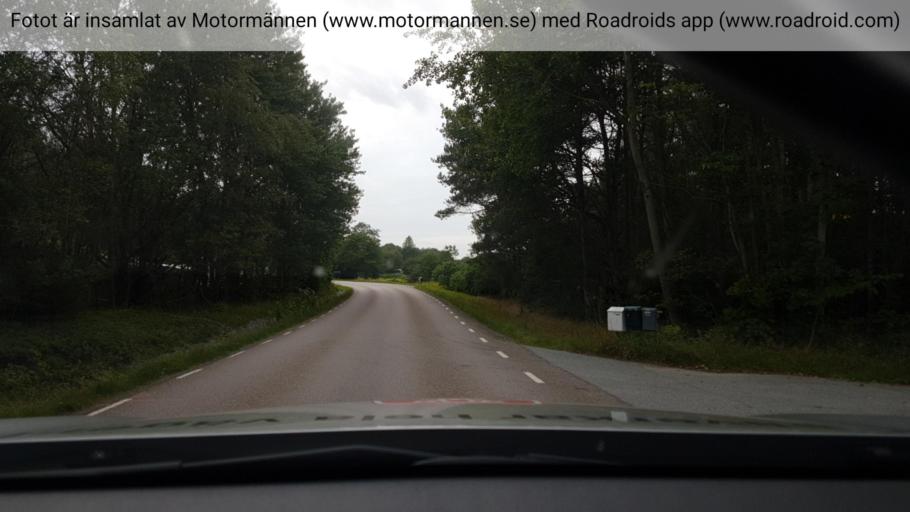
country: SE
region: Vaestra Goetaland
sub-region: Tanums Kommun
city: Grebbestad
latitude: 58.6365
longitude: 11.2913
